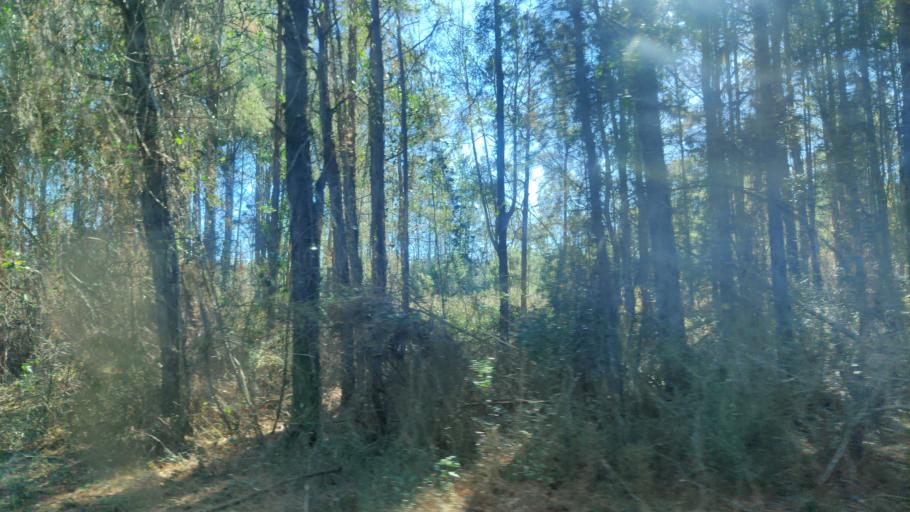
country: US
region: Mississippi
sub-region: Jones County
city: Ellisville
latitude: 31.5466
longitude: -89.3308
